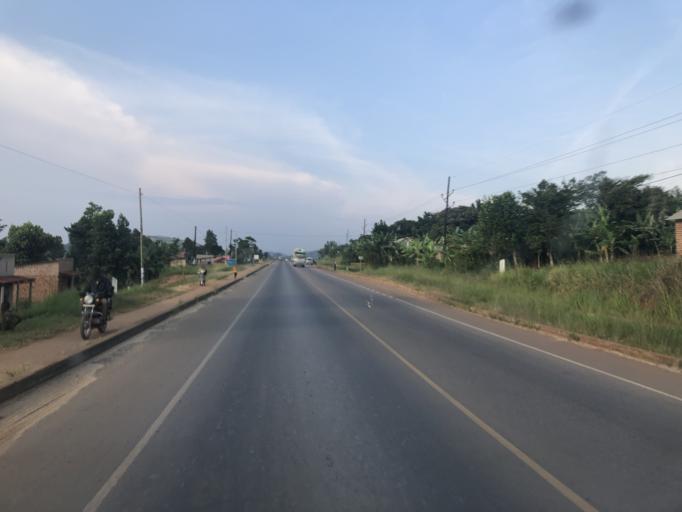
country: UG
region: Central Region
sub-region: Mpigi District
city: Mpigi
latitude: 0.1777
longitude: 32.2777
